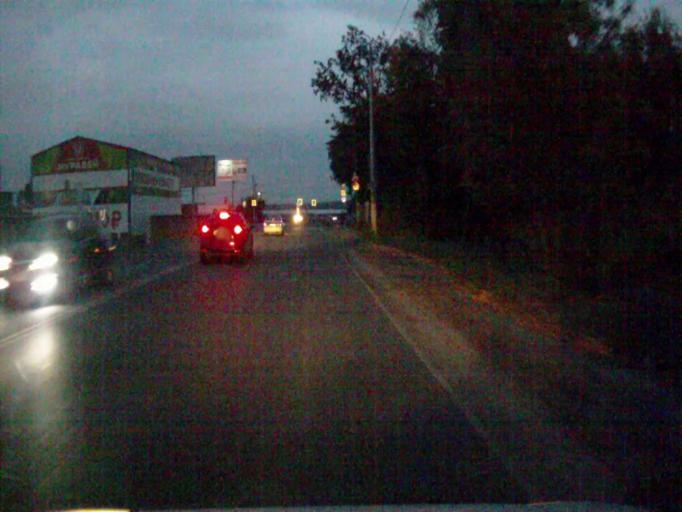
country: RU
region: Chelyabinsk
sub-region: Gorod Chelyabinsk
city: Chelyabinsk
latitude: 55.1498
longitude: 61.3031
